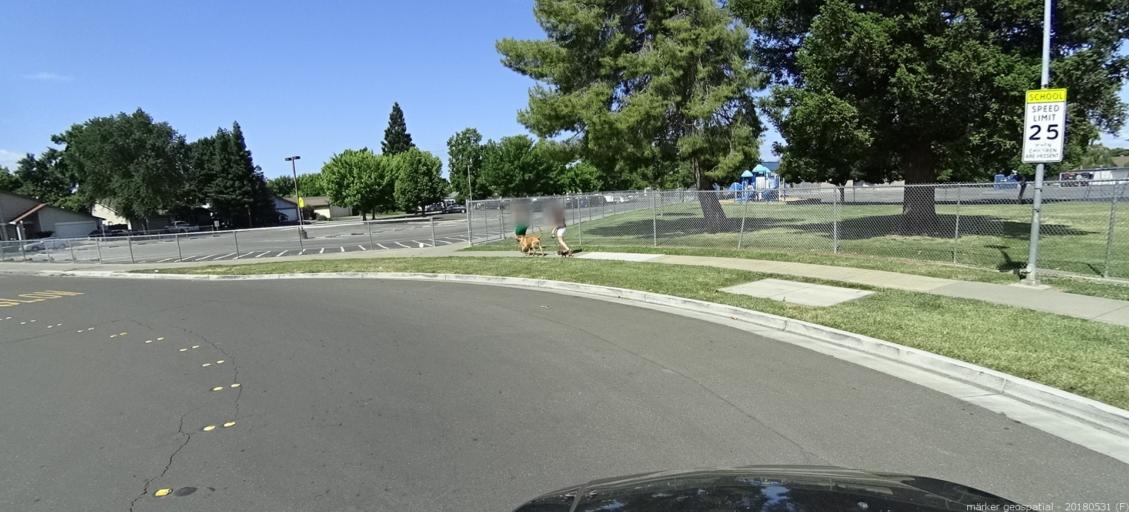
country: US
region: California
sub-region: Sacramento County
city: Sacramento
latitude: 38.6213
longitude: -121.5055
